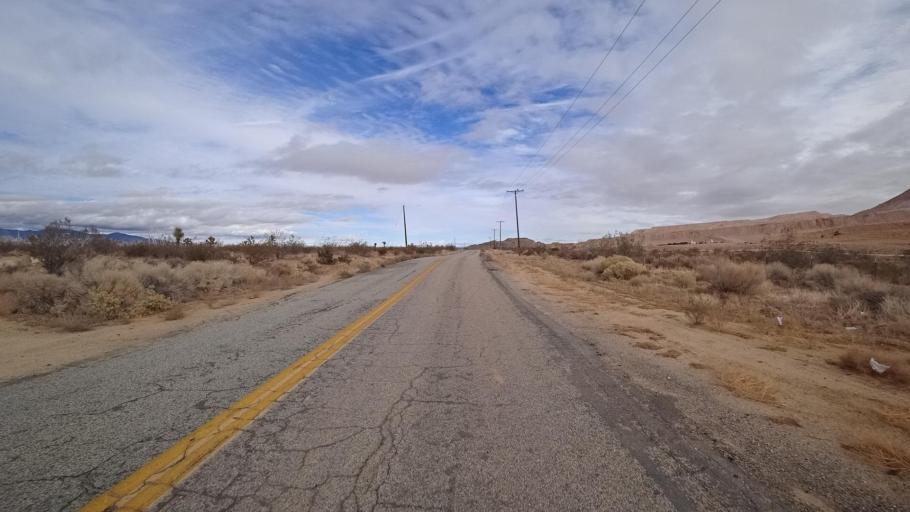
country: US
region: California
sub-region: Kern County
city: Mojave
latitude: 34.9929
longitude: -118.2040
